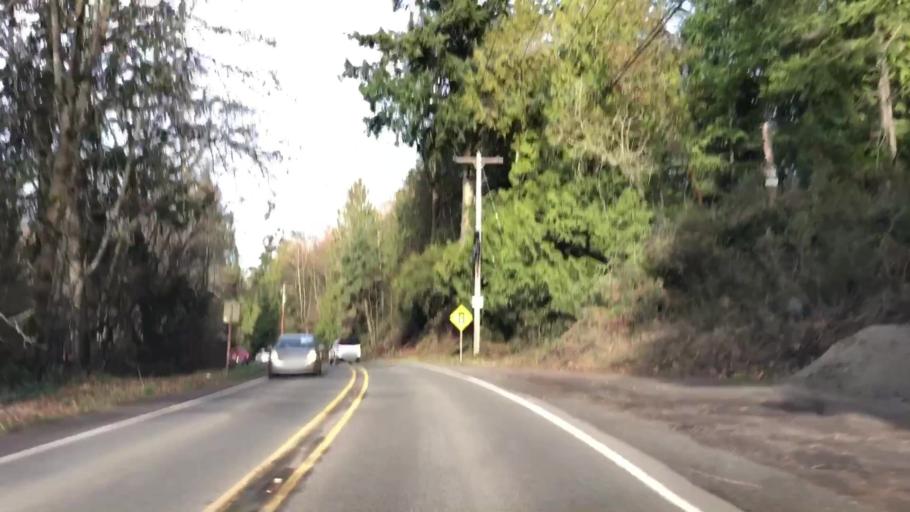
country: US
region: Washington
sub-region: Kitsap County
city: Indianola
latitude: 47.7728
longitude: -122.5551
